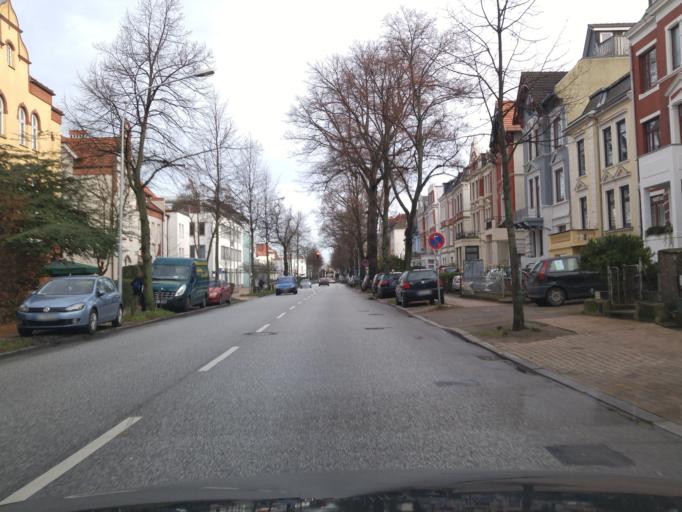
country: DE
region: Schleswig-Holstein
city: Luebeck
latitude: 53.8643
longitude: 10.6684
